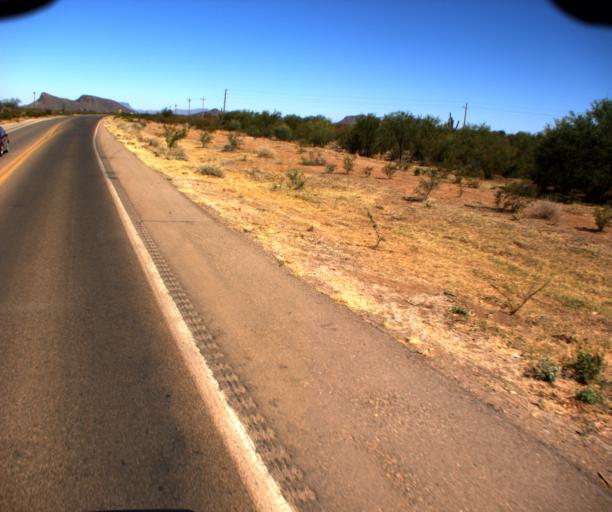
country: US
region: Arizona
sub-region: Pima County
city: Sells
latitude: 31.9239
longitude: -111.8966
